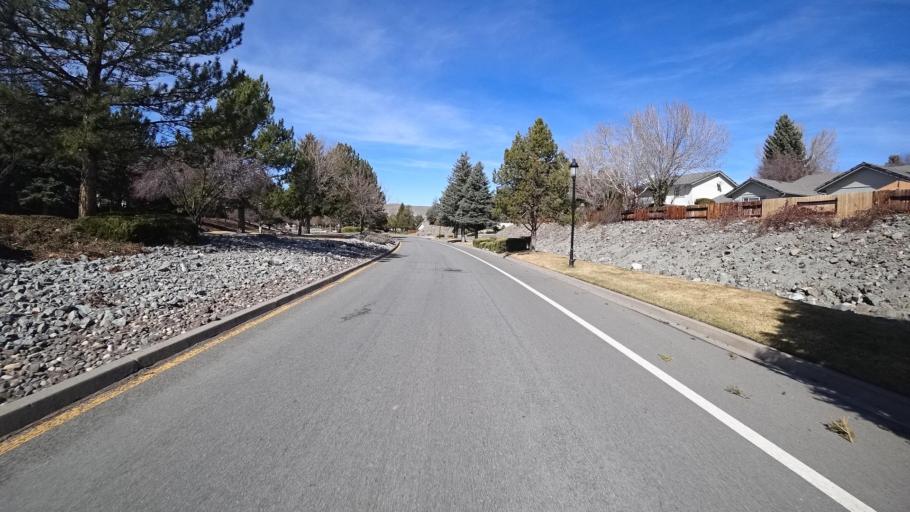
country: US
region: Nevada
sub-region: Washoe County
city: Spanish Springs
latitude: 39.5855
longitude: -119.7097
